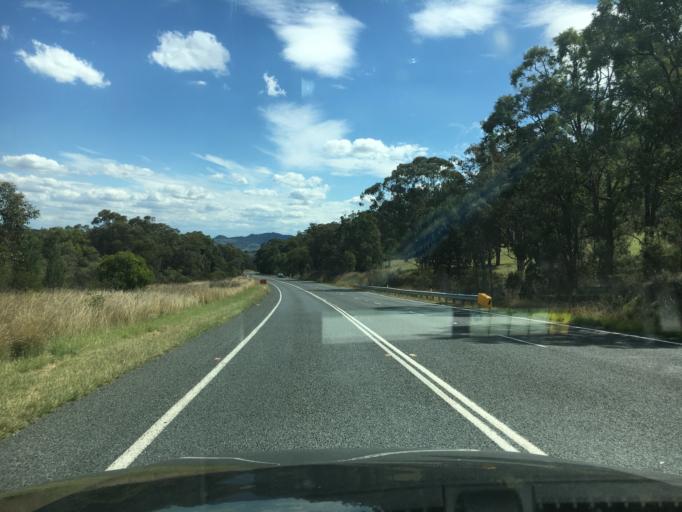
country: AU
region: New South Wales
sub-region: Liverpool Plains
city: Quirindi
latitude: -31.4457
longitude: 150.8731
